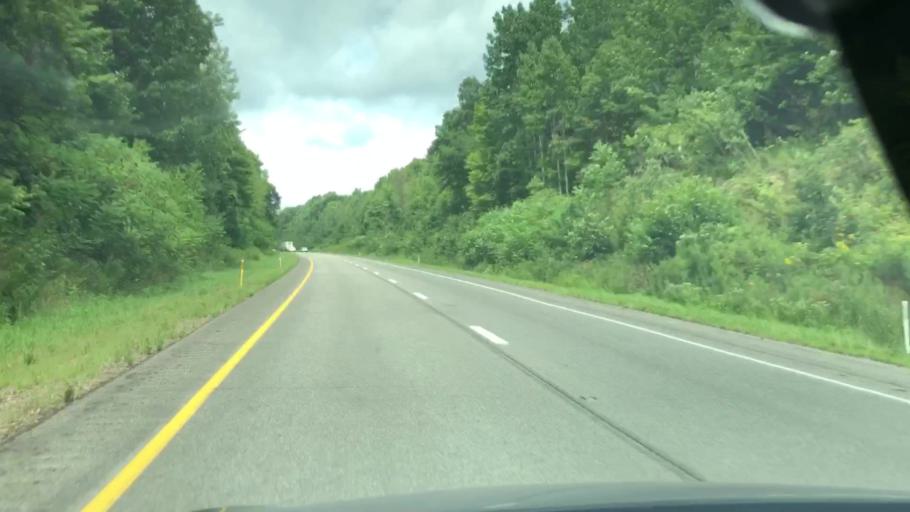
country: US
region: Pennsylvania
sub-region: Crawford County
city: Meadville
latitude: 41.7054
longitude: -80.1983
